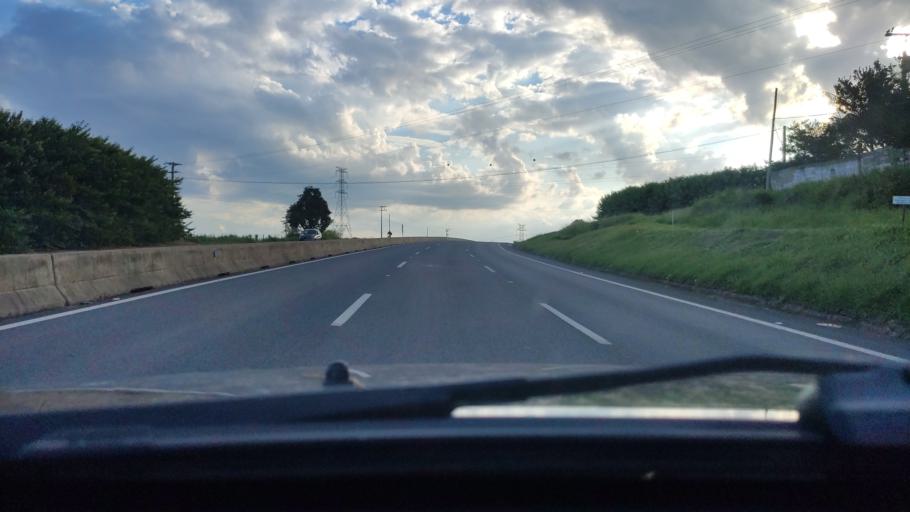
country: BR
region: Sao Paulo
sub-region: Mogi-Mirim
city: Mogi Mirim
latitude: -22.4497
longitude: -47.0608
